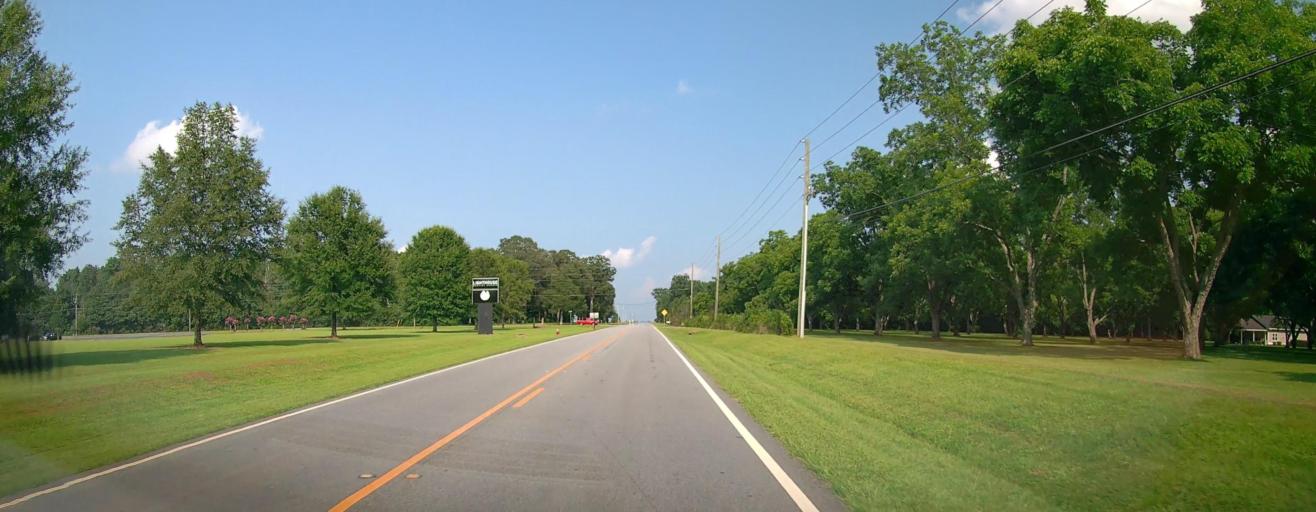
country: US
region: Georgia
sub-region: Houston County
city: Centerville
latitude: 32.6594
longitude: -83.6913
